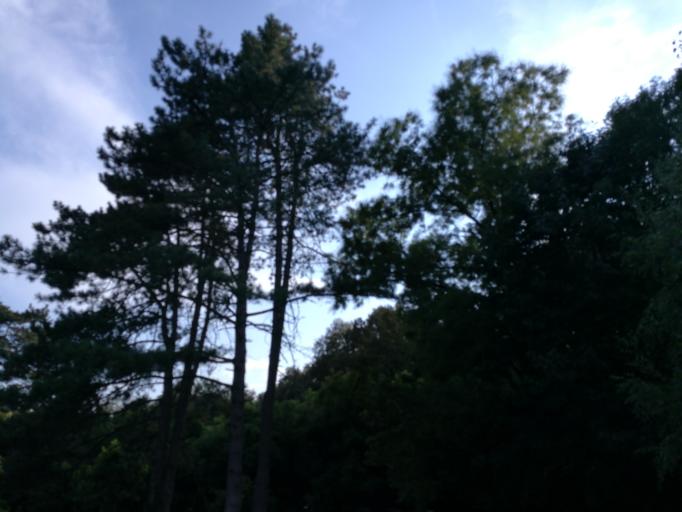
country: RO
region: Ilfov
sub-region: Comuna Otopeni
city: Otopeni
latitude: 44.5180
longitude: 26.0904
